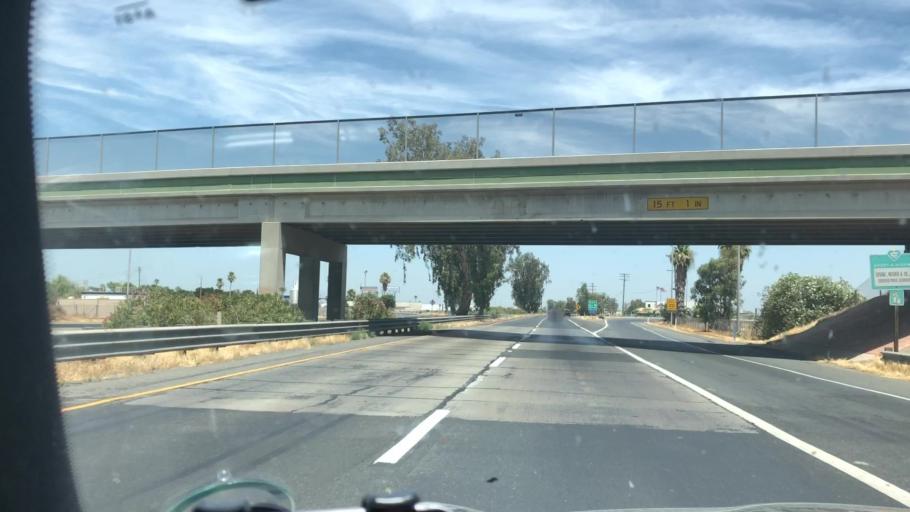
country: US
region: California
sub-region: Tulare County
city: Tulare
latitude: 36.1512
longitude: -119.3307
